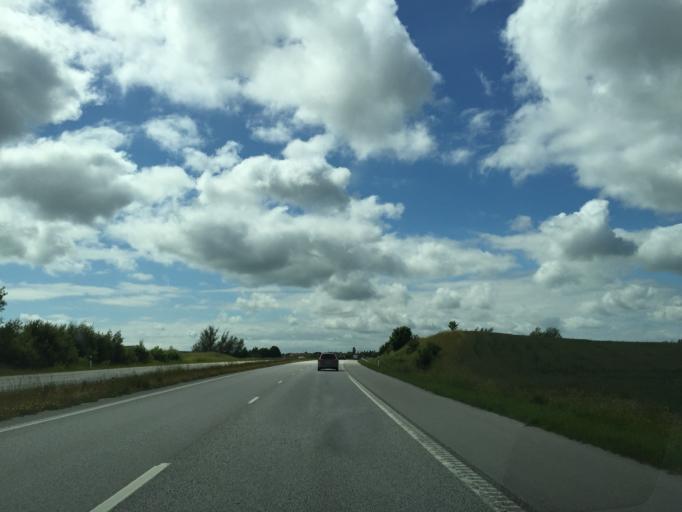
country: SE
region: Skane
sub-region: Svedala Kommun
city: Svedala
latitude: 55.5143
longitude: 13.2625
